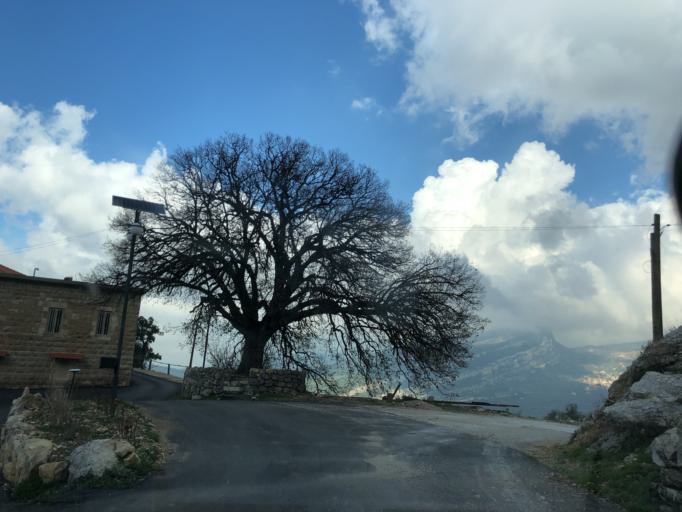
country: LB
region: Liban-Nord
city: Amioun
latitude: 34.2161
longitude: 35.8295
